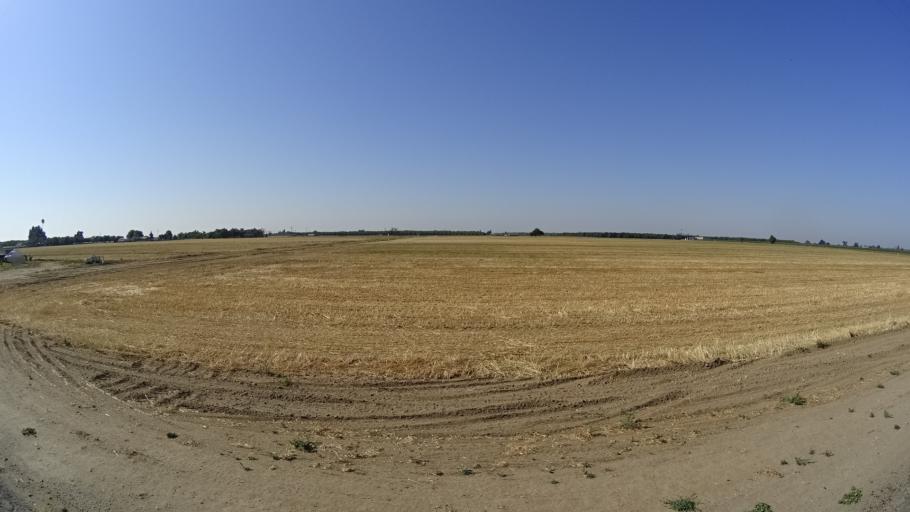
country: US
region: California
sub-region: Kings County
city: Lucerne
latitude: 36.3864
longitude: -119.6139
